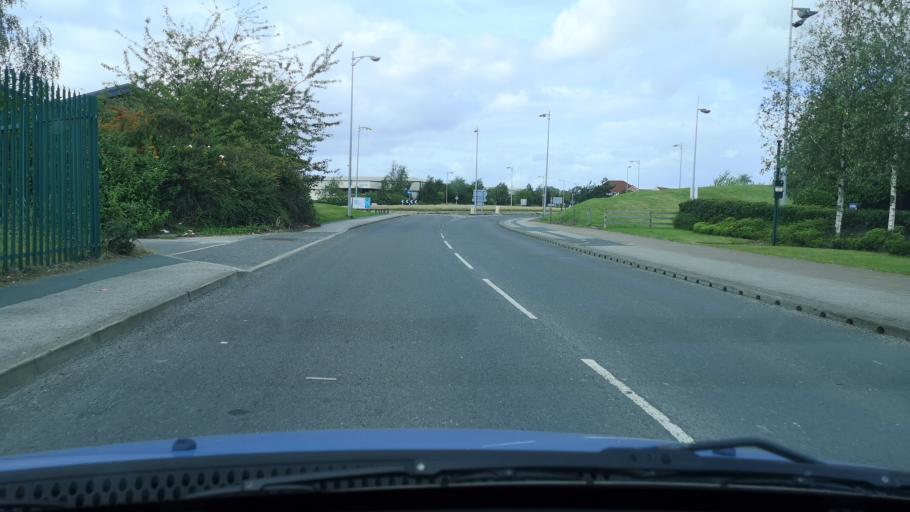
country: GB
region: England
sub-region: City and Borough of Wakefield
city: Castleford
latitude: 53.7101
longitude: -1.3440
